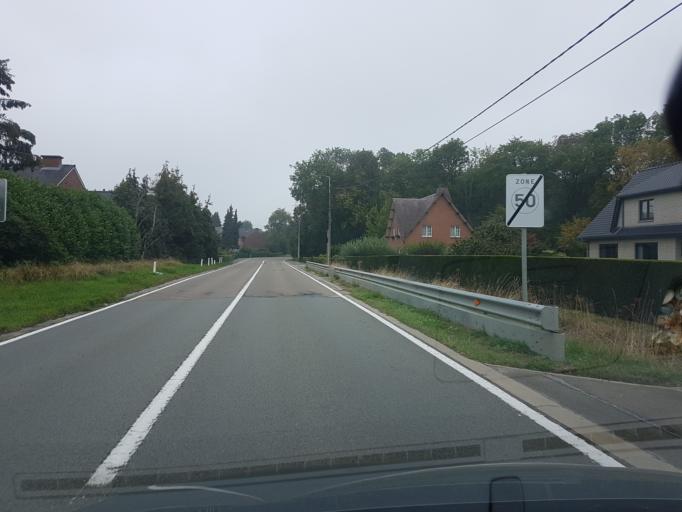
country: BE
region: Wallonia
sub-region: Province de Namur
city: Andenne
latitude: 50.4694
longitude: 5.0972
